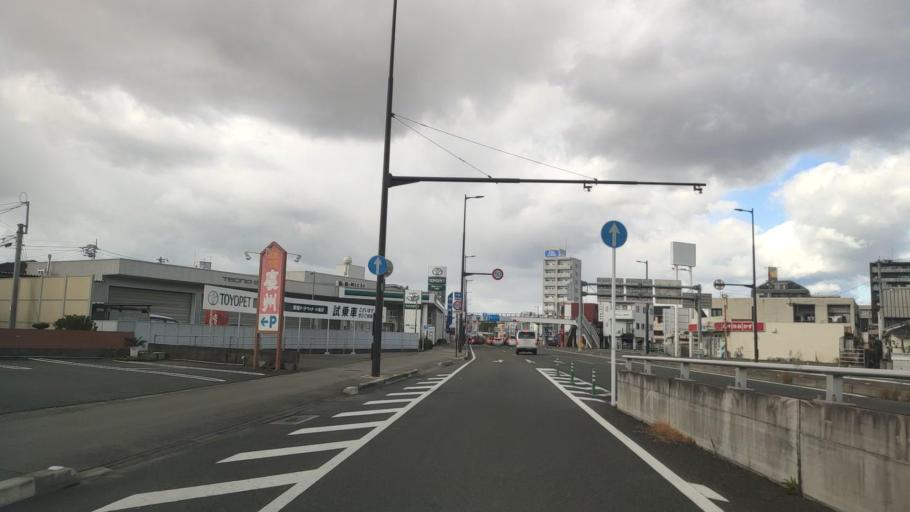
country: JP
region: Ehime
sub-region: Shikoku-chuo Shi
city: Matsuyama
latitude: 33.8283
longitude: 132.7817
